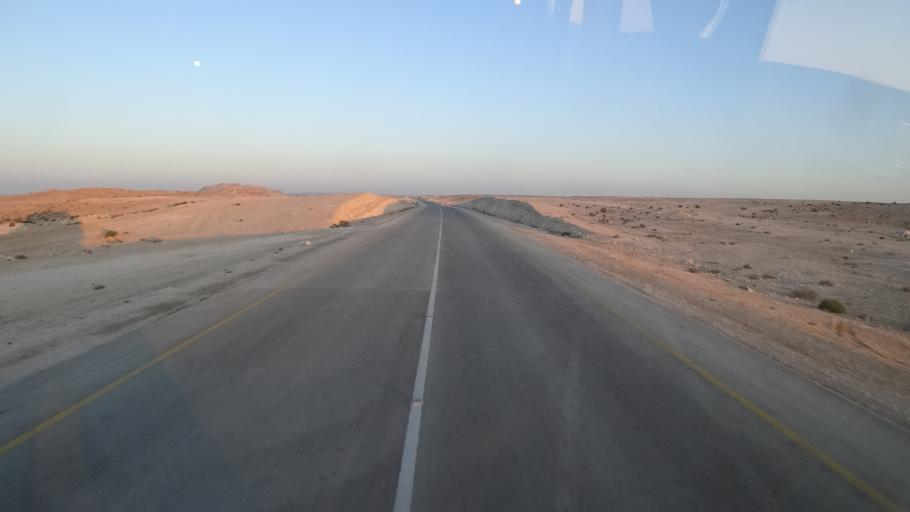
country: YE
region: Al Mahrah
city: Hawf
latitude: 16.9508
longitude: 53.3490
